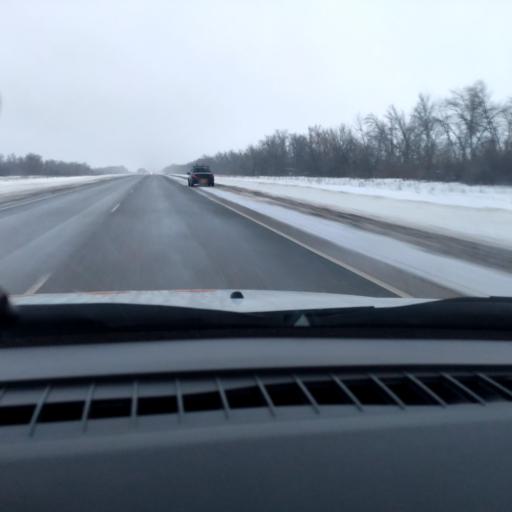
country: RU
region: Samara
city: Dubovyy Umet
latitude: 53.0416
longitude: 50.2071
